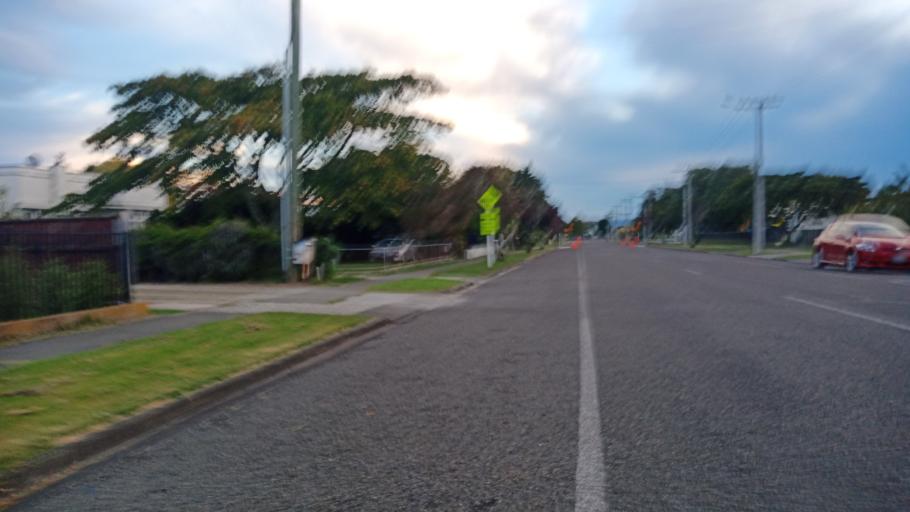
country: NZ
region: Gisborne
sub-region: Gisborne District
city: Gisborne
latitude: -38.6504
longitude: 178.0022
